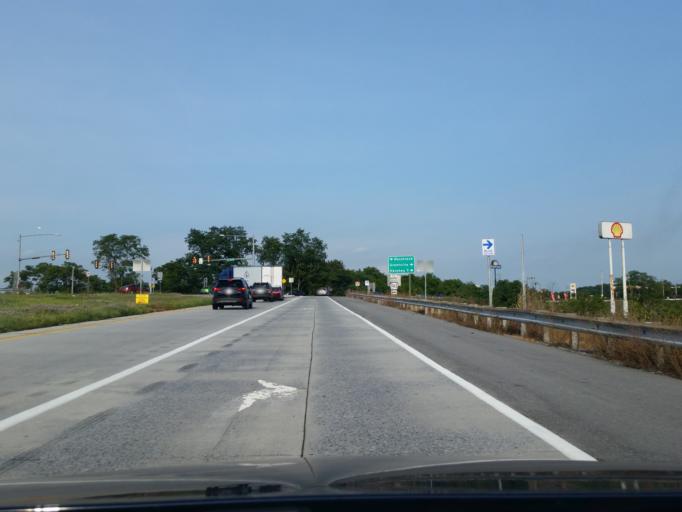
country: US
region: Pennsylvania
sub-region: Dauphin County
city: Skyline View
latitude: 40.3792
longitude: -76.6611
